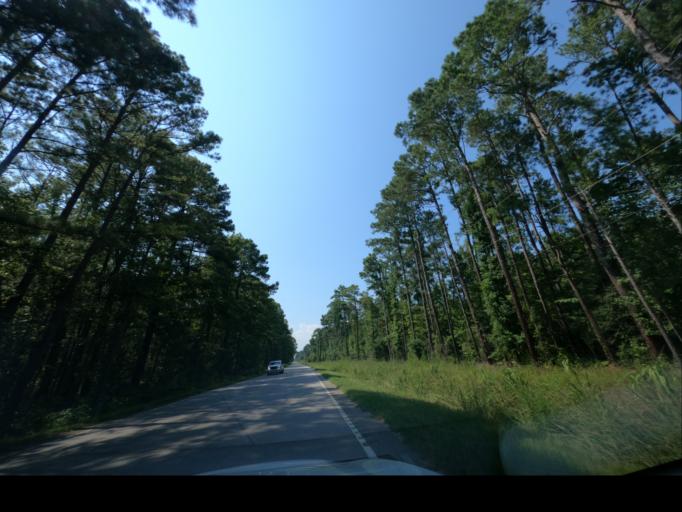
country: US
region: South Carolina
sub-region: Richland County
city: Hopkins
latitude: 33.9033
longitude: -80.9274
